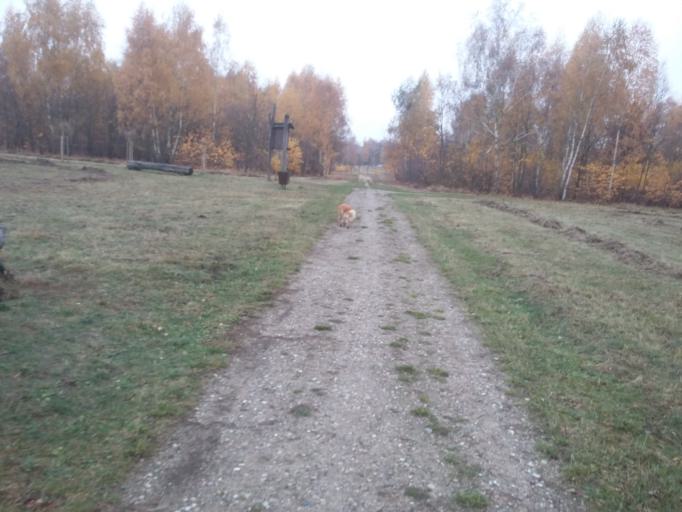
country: PL
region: Lodz Voivodeship
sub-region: Powiat pabianicki
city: Ksawerow
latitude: 51.7307
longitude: 19.3846
